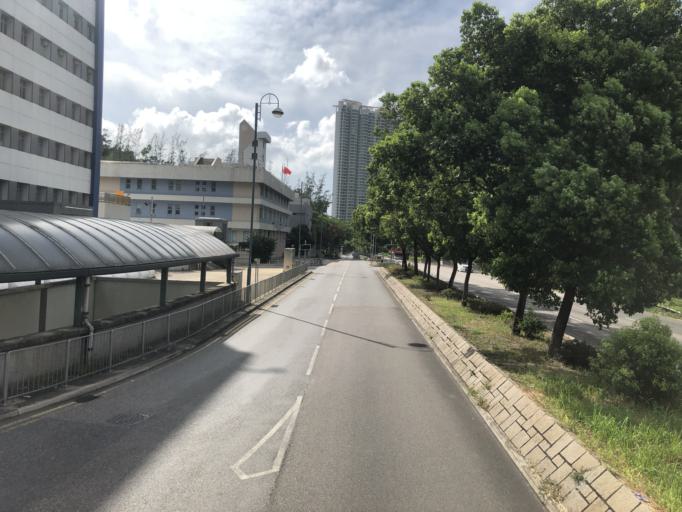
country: HK
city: Tai O
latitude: 22.2847
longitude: 113.9427
